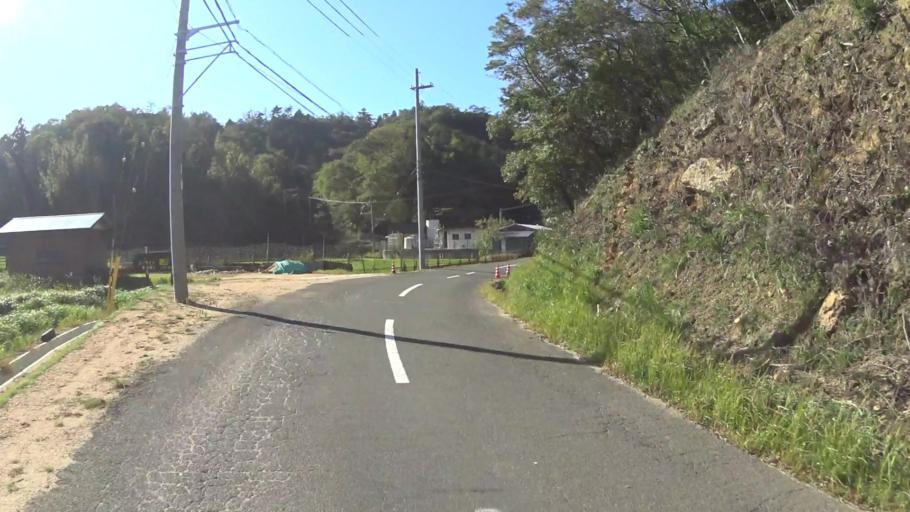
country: JP
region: Hyogo
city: Toyooka
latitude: 35.6381
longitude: 134.8894
